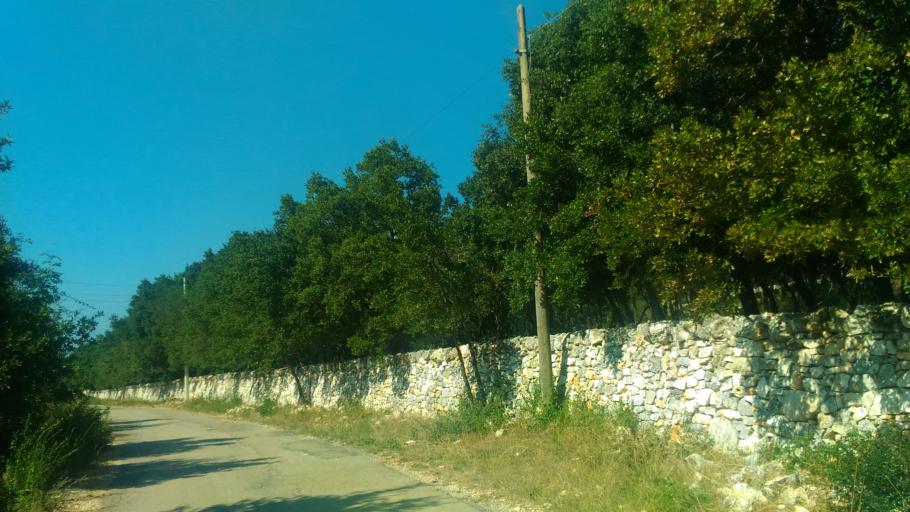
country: IT
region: Apulia
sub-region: Provincia di Bari
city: Noci
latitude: 40.8167
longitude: 17.1776
